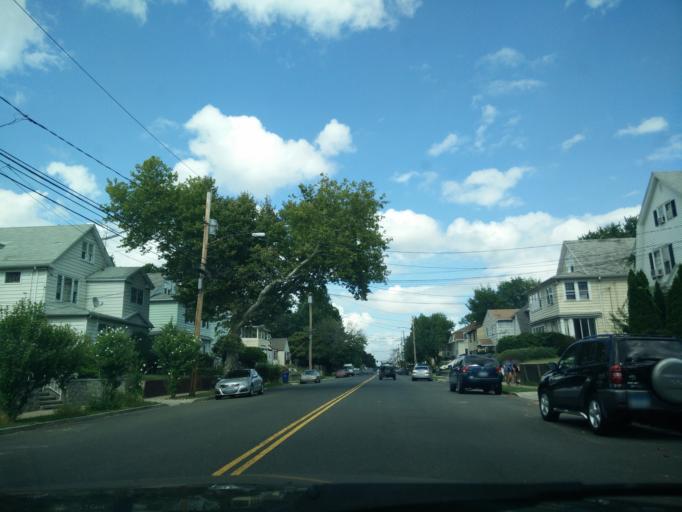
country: US
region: Connecticut
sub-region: Fairfield County
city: Bridgeport
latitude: 41.1924
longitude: -73.2092
